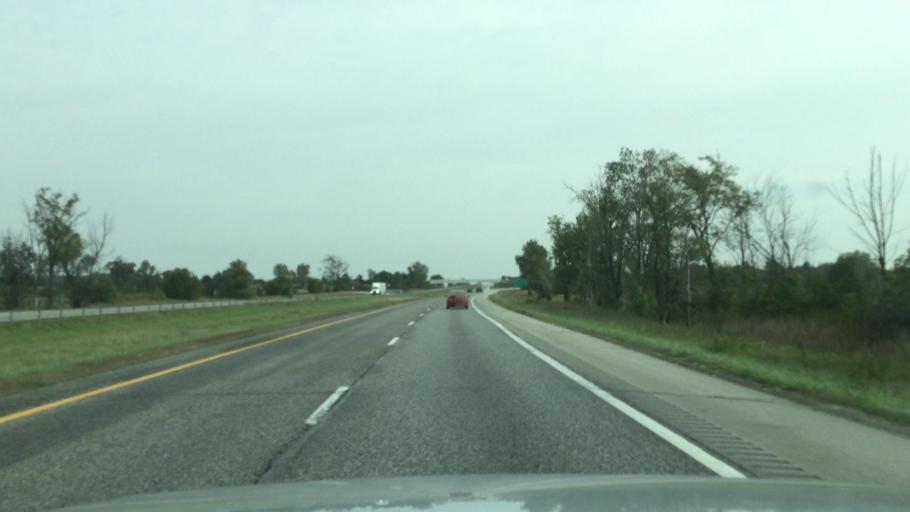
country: US
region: Michigan
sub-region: Shiawassee County
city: Corunna
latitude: 42.8913
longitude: -84.1020
